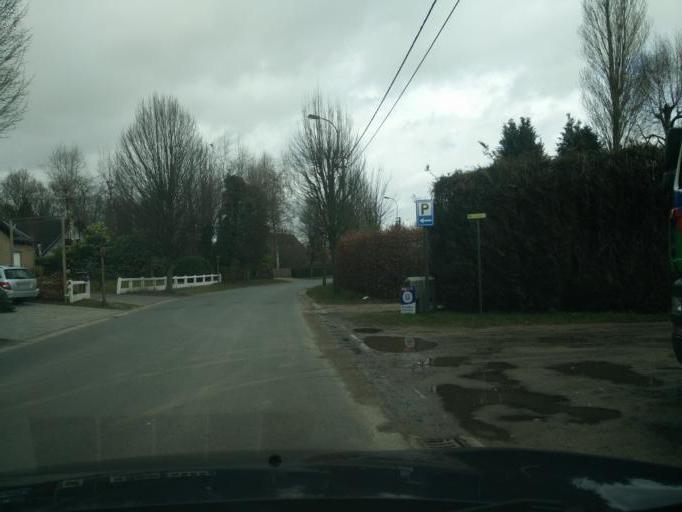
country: BE
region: Flanders
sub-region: Provincie Oost-Vlaanderen
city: Melle
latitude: 51.0299
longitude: 3.8113
